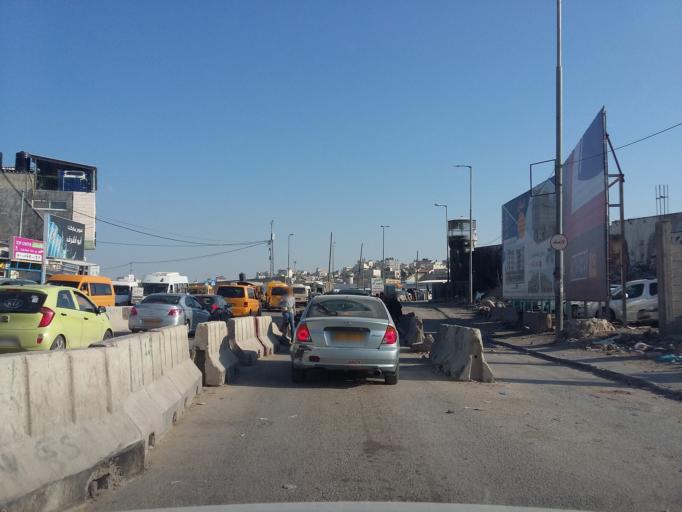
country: PS
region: West Bank
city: Ar Ram wa Dahiyat al Barid
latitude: 31.8640
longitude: 35.2275
